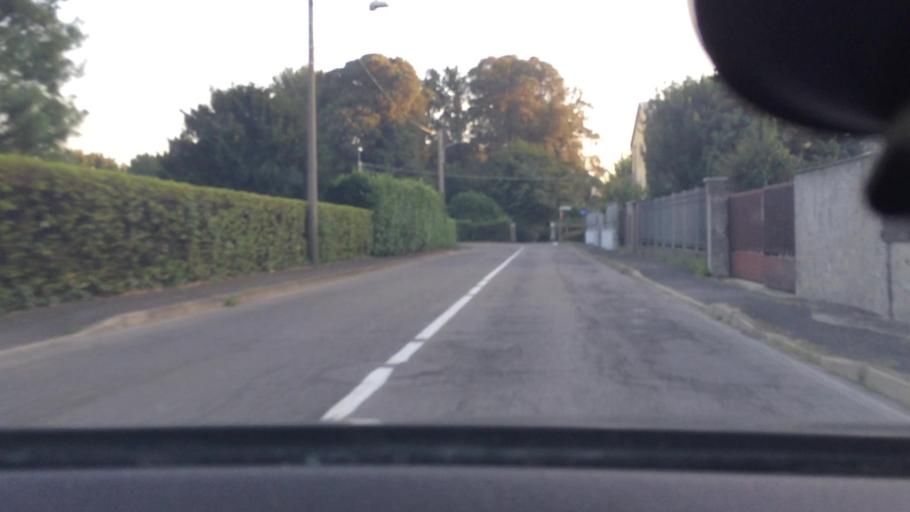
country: IT
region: Lombardy
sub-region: Provincia di Como
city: Rovello Porro
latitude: 45.6511
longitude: 9.0441
